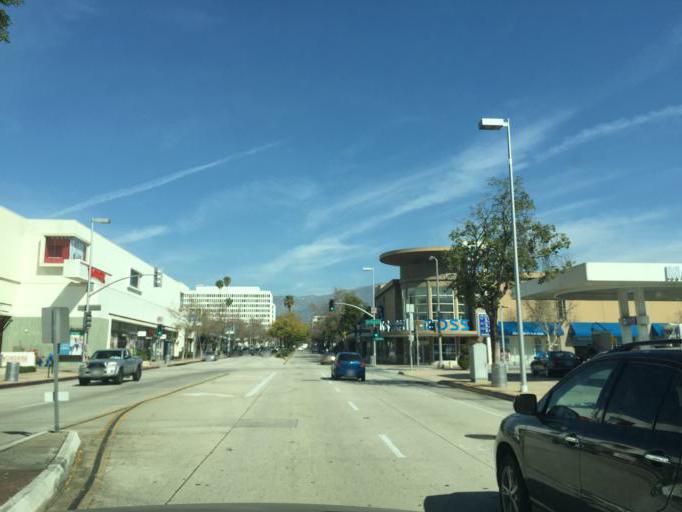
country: US
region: California
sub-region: Los Angeles County
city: Pasadena
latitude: 34.1374
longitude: -118.1323
